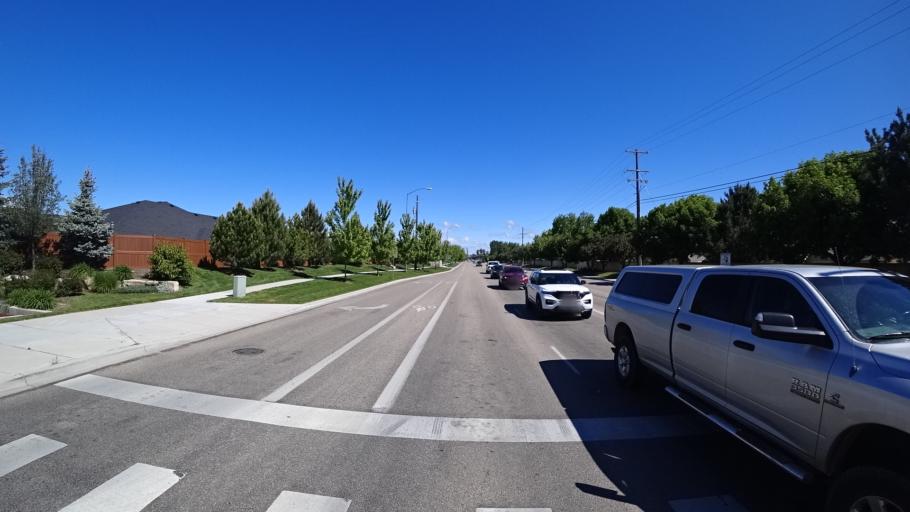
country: US
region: Idaho
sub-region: Ada County
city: Meridian
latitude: 43.6340
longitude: -116.3746
